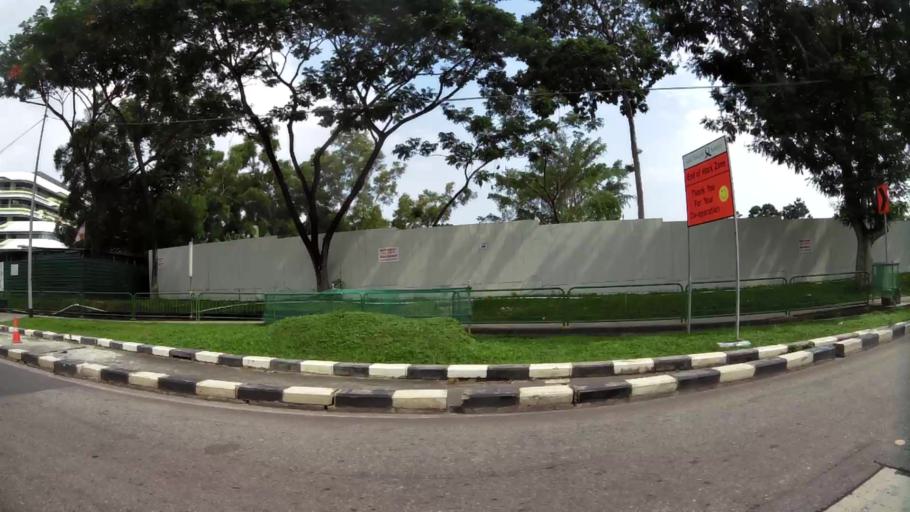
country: SG
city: Singapore
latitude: 1.3394
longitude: 103.9609
